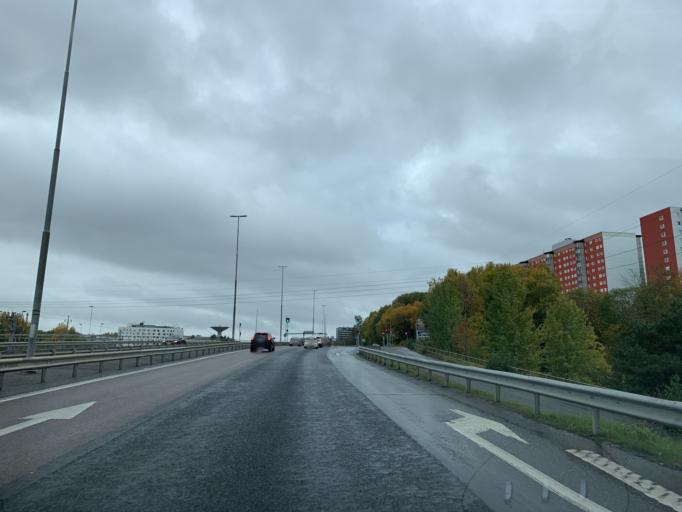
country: SE
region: Stockholm
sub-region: Huddinge Kommun
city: Huddinge
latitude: 59.2235
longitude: 17.9527
